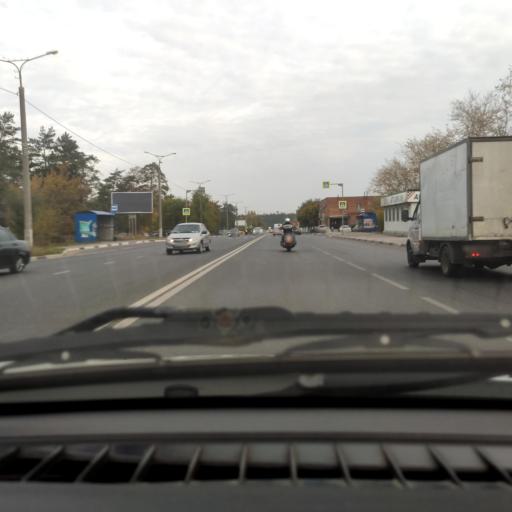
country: RU
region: Samara
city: Zhigulevsk
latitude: 53.4943
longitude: 49.4738
